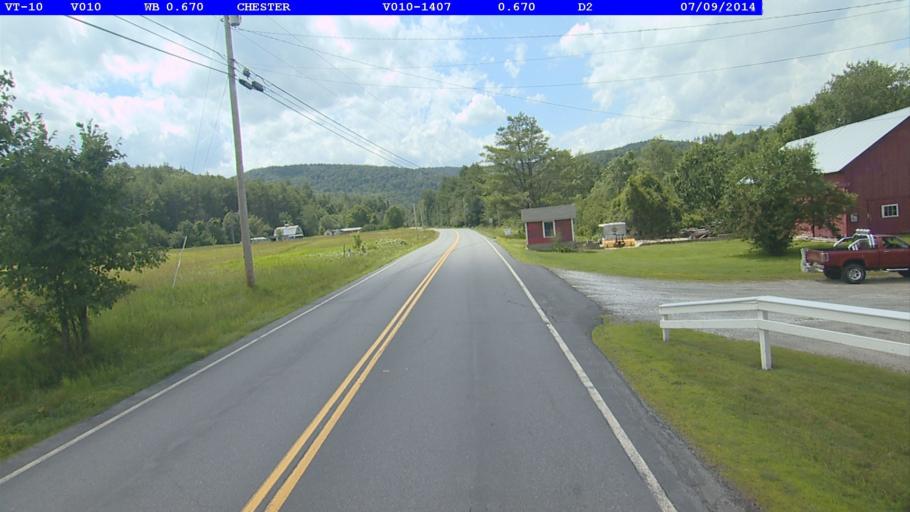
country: US
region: Vermont
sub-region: Windsor County
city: Chester
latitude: 43.3272
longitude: -72.5945
